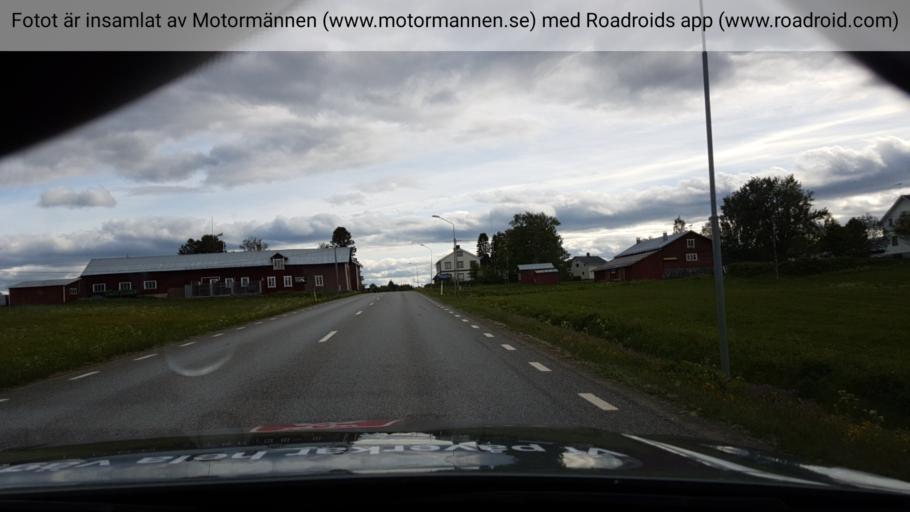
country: SE
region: Jaemtland
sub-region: Stroemsunds Kommun
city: Stroemsund
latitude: 63.4988
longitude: 15.2580
